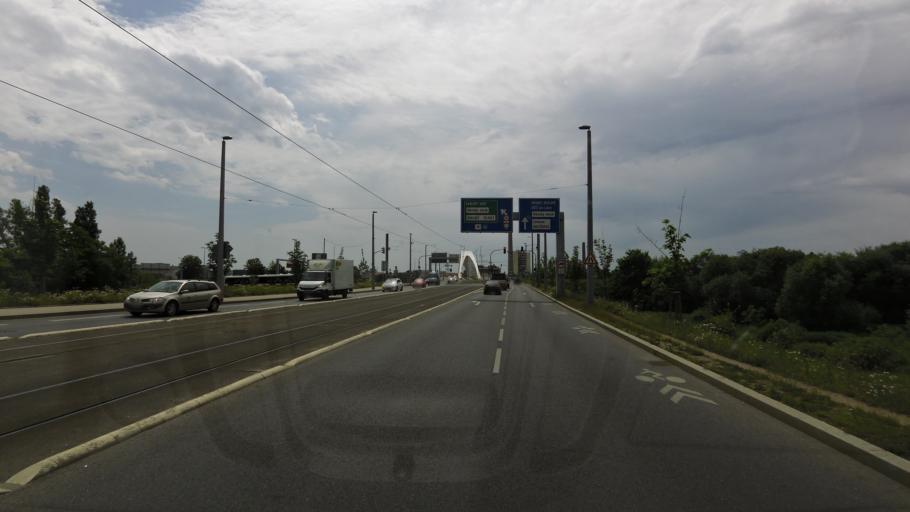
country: CZ
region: Praha
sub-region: Praha 8
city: Karlin
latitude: 50.1155
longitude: 14.4348
